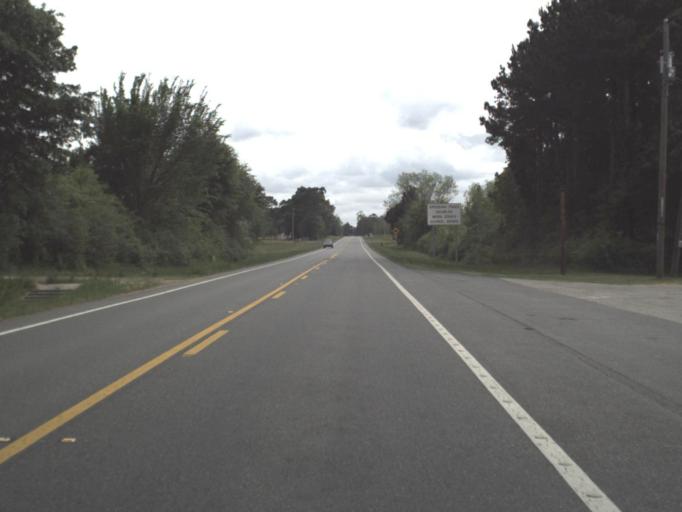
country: US
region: Alabama
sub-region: Escambia County
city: East Brewton
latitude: 30.9940
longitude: -87.0375
